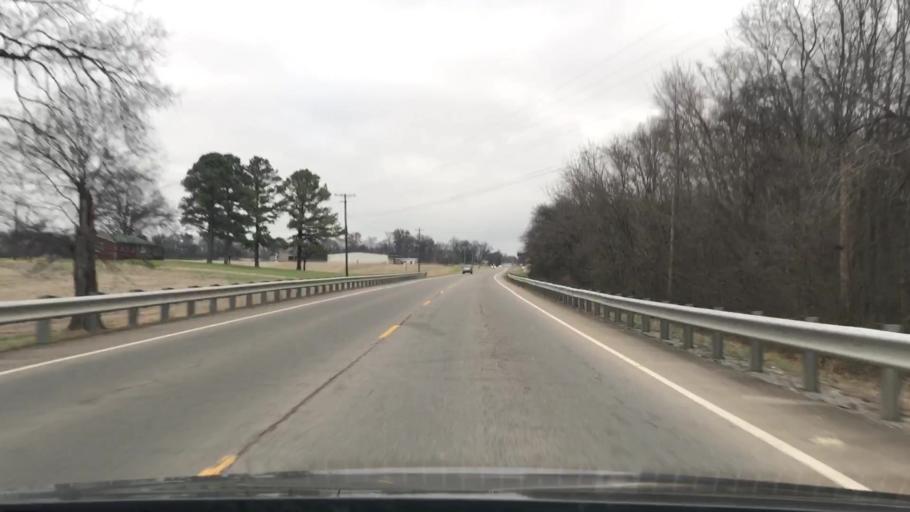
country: US
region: Kentucky
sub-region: Todd County
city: Guthrie
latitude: 36.6361
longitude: -87.2111
